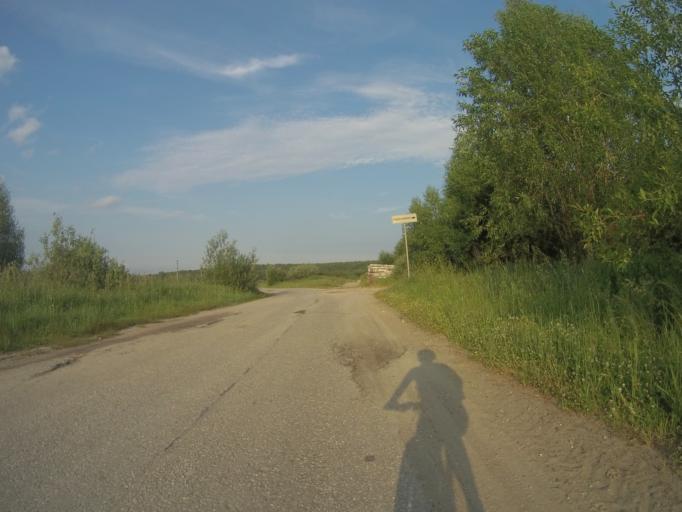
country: RU
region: Vladimir
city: Orgtrud
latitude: 56.0782
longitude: 40.5608
